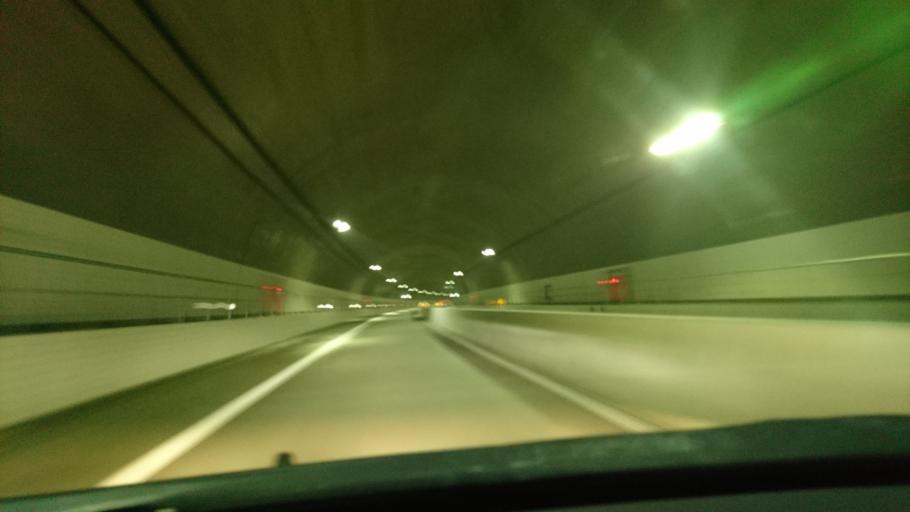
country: JP
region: Iwate
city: Miyako
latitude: 39.8105
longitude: 141.9573
